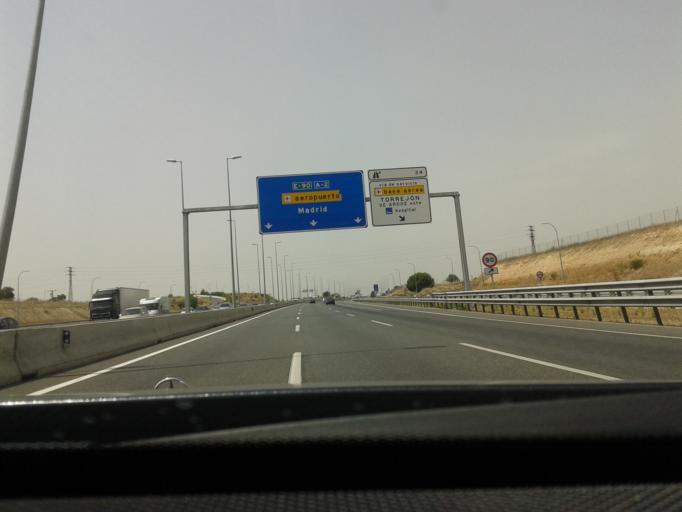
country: ES
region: Madrid
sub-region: Provincia de Madrid
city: Torrejon de Ardoz
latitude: 40.4705
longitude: -3.4271
